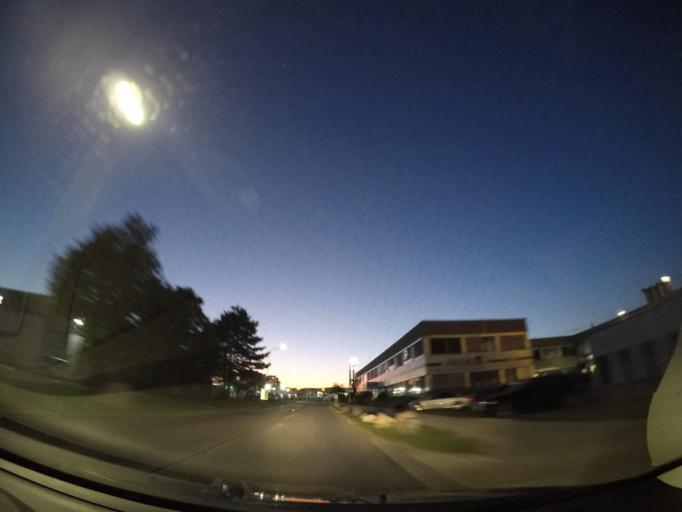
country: AT
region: Lower Austria
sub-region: Politischer Bezirk Modling
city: Wiener Neudorf
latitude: 48.0767
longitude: 16.3264
